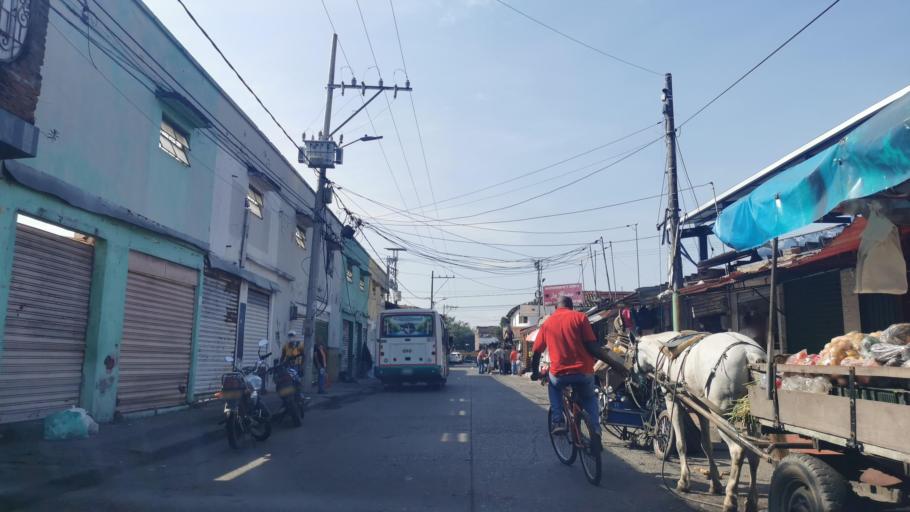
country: CO
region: Valle del Cauca
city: Jamundi
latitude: 3.2609
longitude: -76.5381
